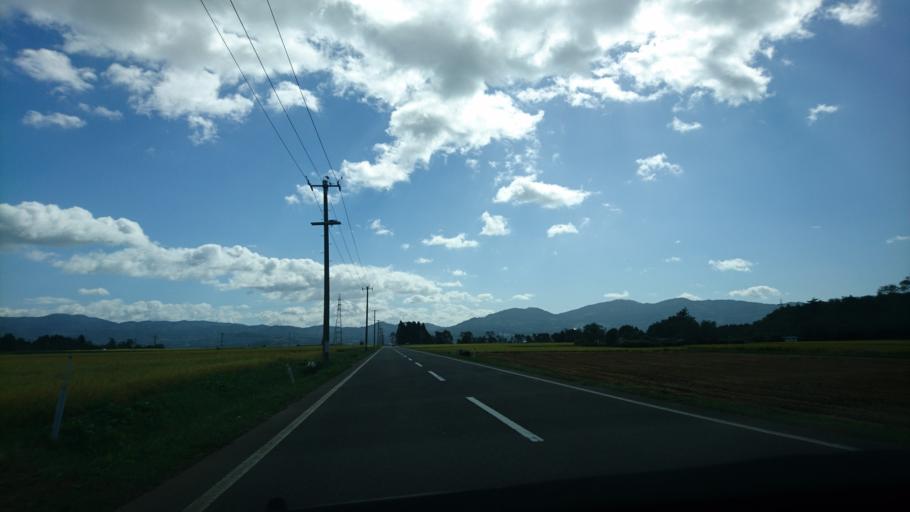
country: JP
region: Iwate
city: Mizusawa
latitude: 39.0726
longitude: 141.1194
